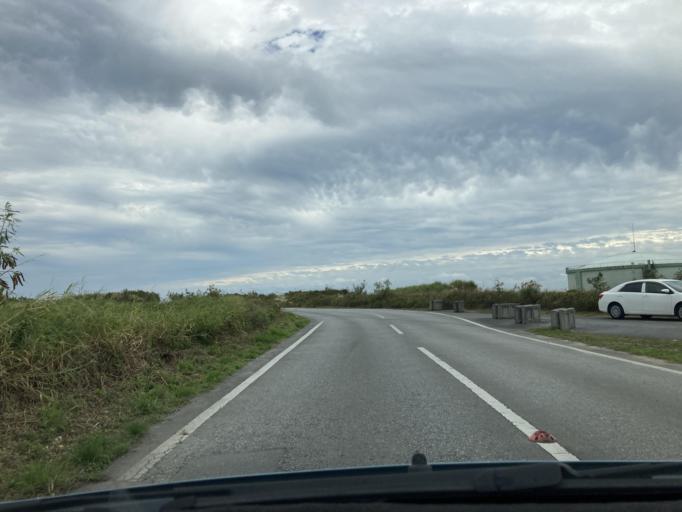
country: JP
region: Okinawa
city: Okinawa
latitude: 26.3871
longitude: 127.7405
